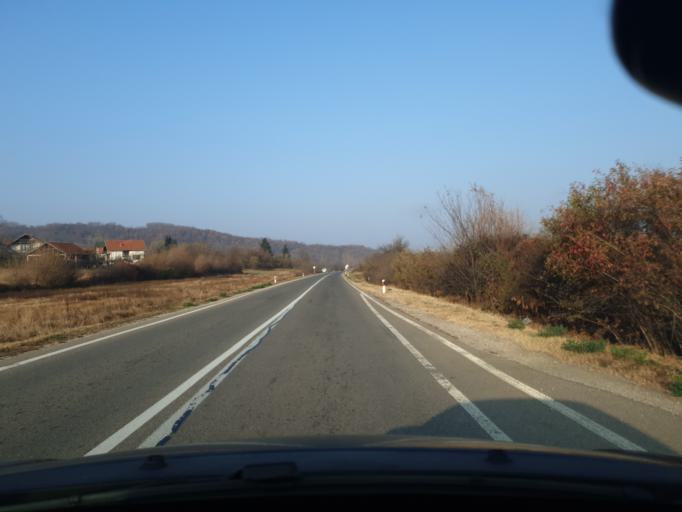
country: RS
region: Central Serbia
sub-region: Jablanicki Okrug
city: Vlasotince
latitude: 42.9147
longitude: 22.0353
